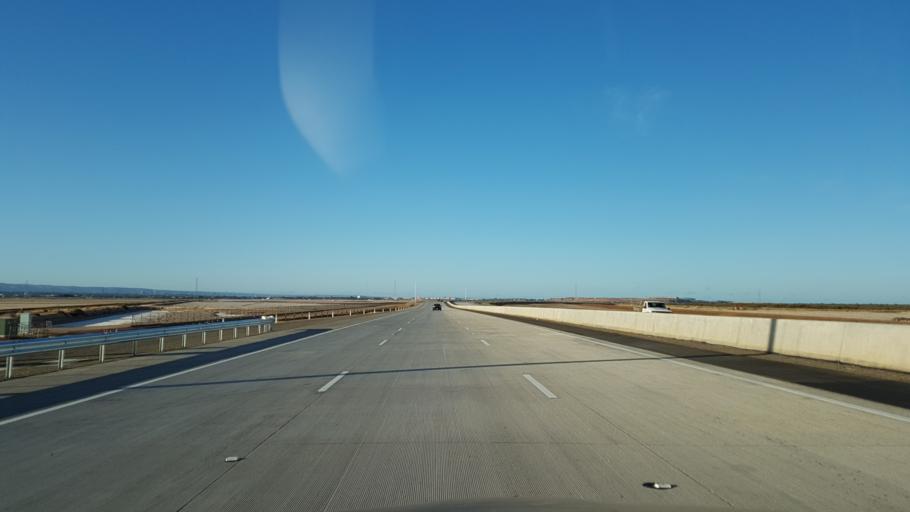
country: AU
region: South Australia
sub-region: Port Adelaide Enfield
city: Enfield
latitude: -34.7959
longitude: 138.5781
